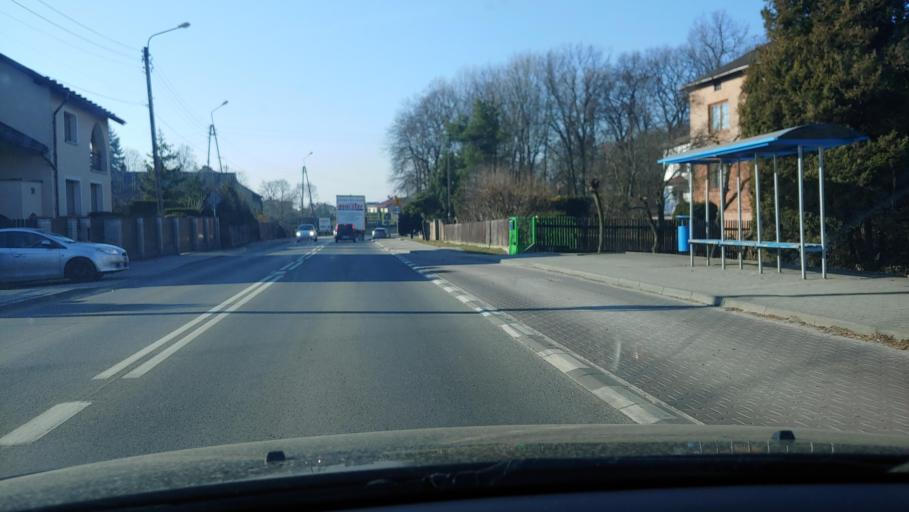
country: PL
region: Lesser Poland Voivodeship
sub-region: Powiat chrzanowski
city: Trzebinia
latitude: 50.1661
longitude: 19.4730
